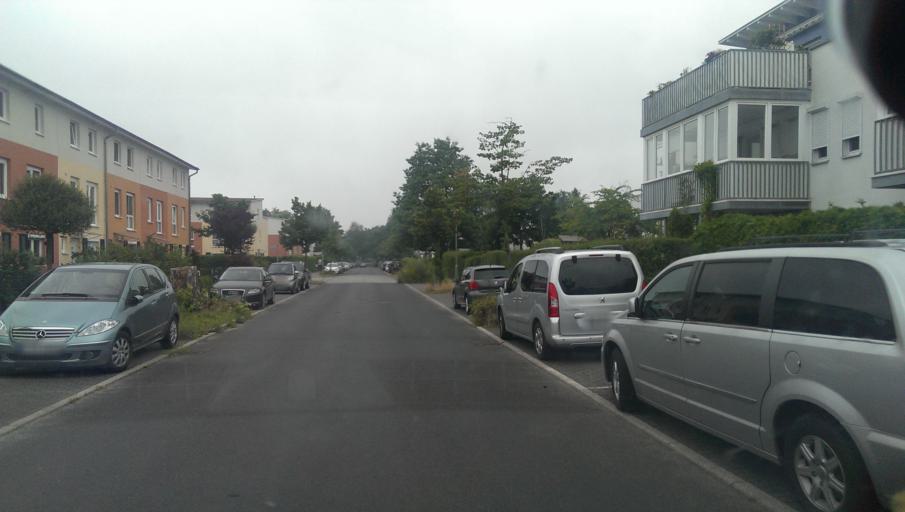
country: DE
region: Berlin
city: Lichterfelde
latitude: 52.4269
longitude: 13.2976
